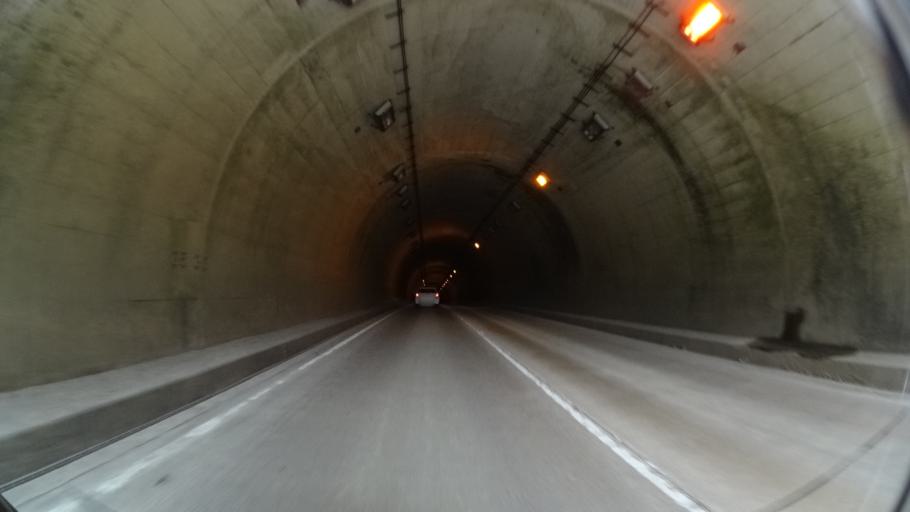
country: JP
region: Hyogo
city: Toyooka
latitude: 35.5045
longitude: 134.8660
